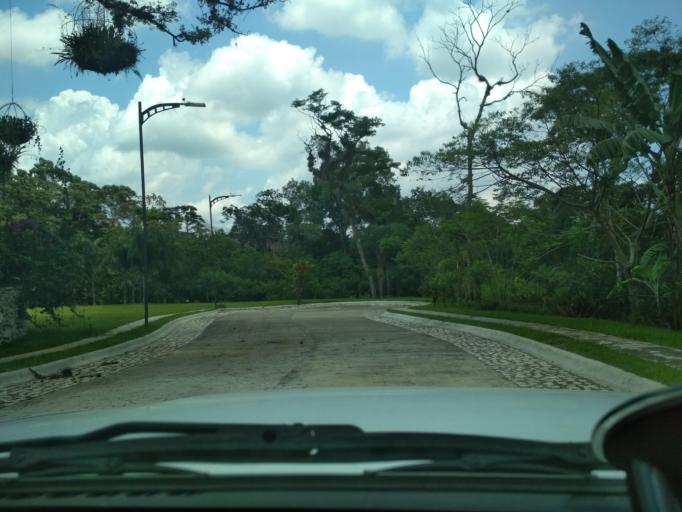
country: MX
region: Veracruz
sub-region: Cordoba
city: San Jose de Abajo [Unidad Habitacional]
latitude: 18.9187
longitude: -96.9535
